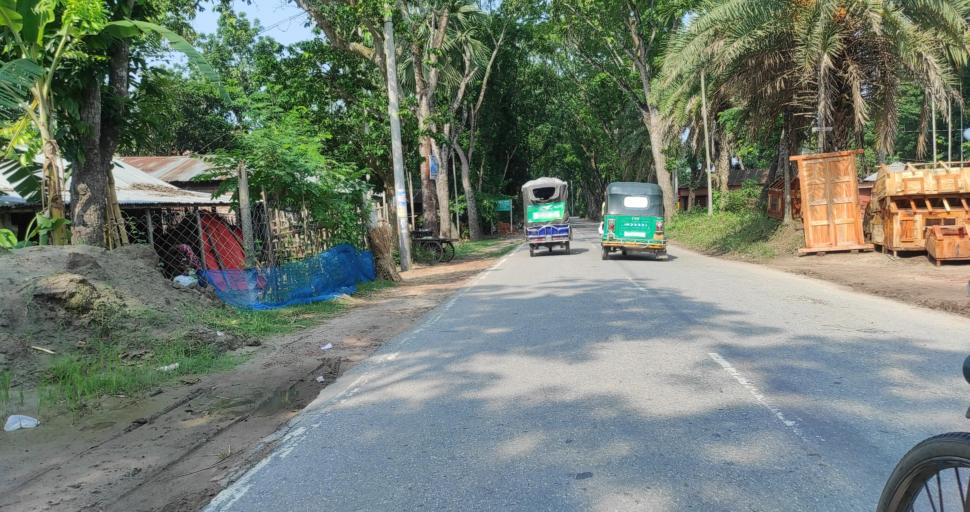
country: BD
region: Rajshahi
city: Ishurdi
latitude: 24.2897
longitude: 89.0754
